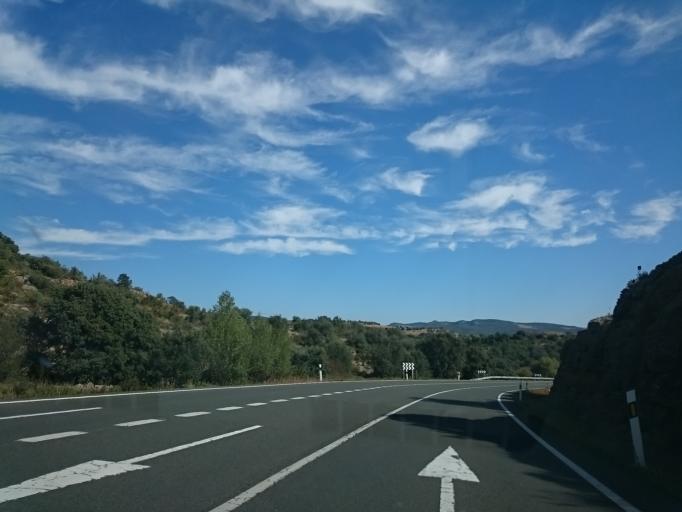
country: ES
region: Aragon
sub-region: Provincia de Huesca
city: Benavarri / Benabarre
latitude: 42.1145
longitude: 0.5400
